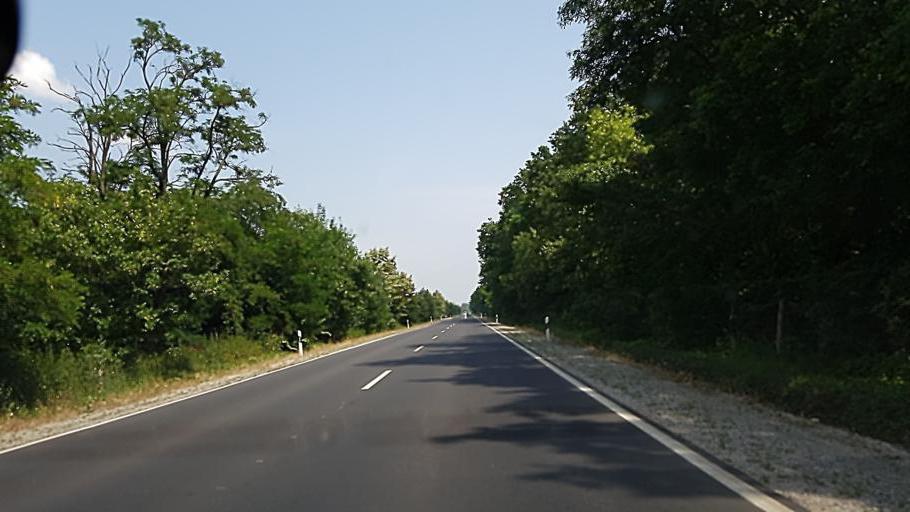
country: HU
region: Heves
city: Besenyotelek
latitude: 47.6762
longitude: 20.5239
